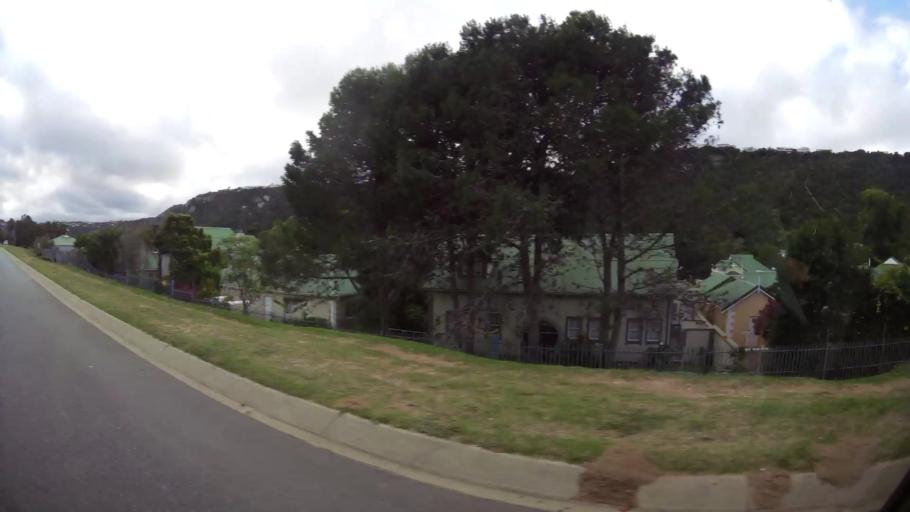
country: ZA
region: Western Cape
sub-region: Eden District Municipality
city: Plettenberg Bay
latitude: -34.0621
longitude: 23.3708
